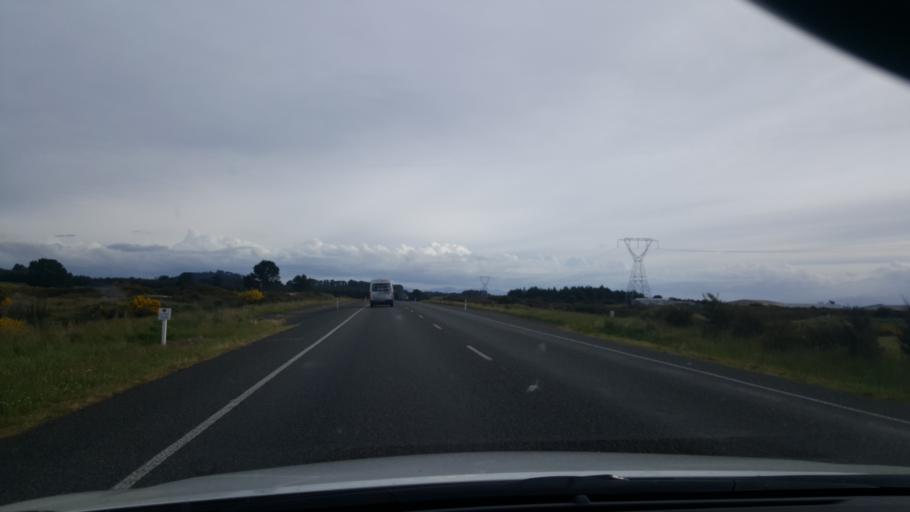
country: NZ
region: Waikato
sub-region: Taupo District
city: Taupo
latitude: -38.6899
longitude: 176.1139
